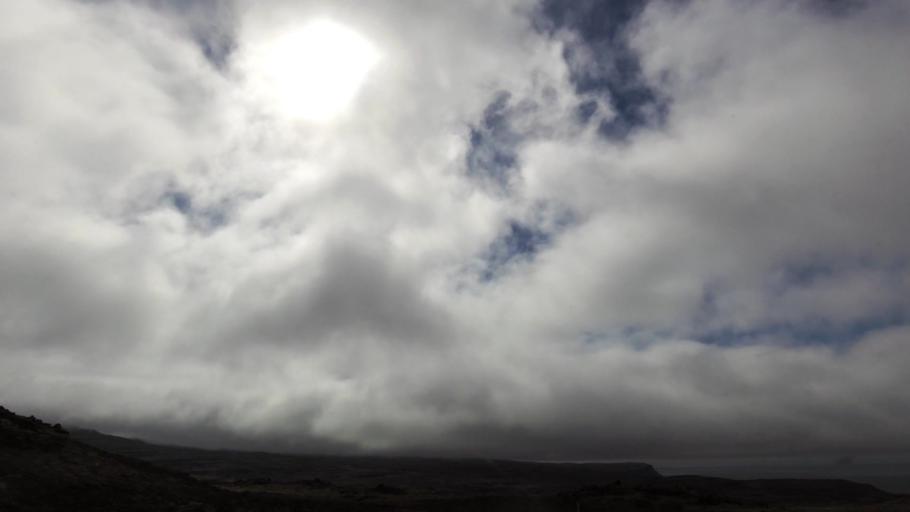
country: IS
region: West
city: Olafsvik
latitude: 65.5448
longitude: -24.2839
